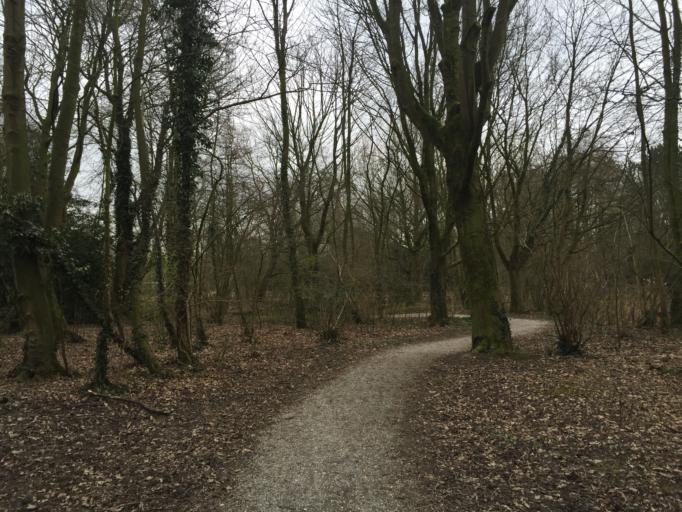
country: NL
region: South Holland
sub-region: Gemeente Leiden
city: Leiden
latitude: 52.1787
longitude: 4.5066
